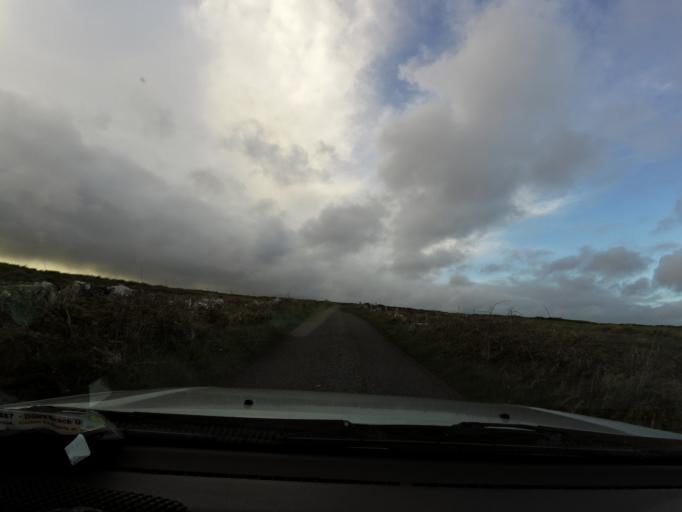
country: IE
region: Munster
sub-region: An Clar
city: Kilrush
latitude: 52.9498
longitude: -9.4437
